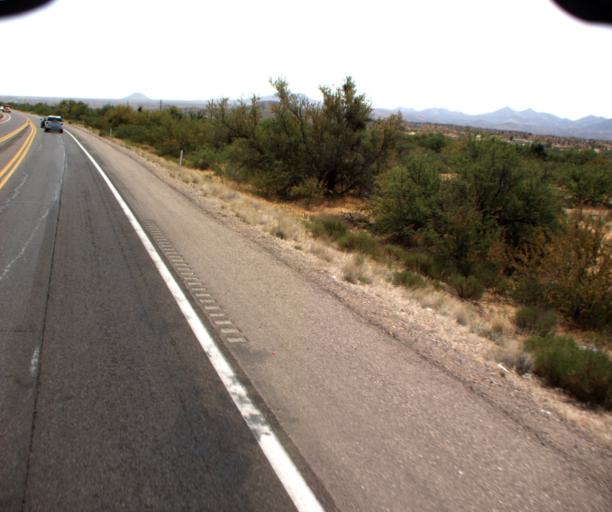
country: US
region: Arizona
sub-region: Gila County
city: Globe
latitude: 33.3594
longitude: -110.6969
